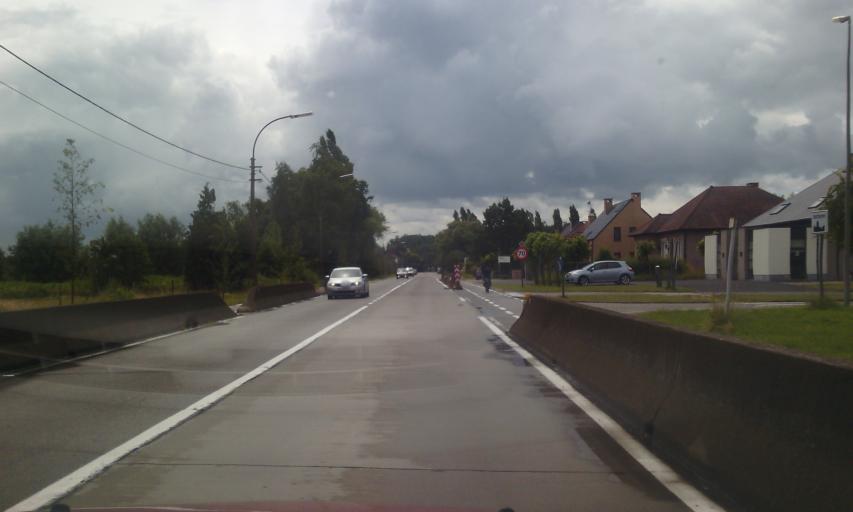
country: BE
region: Flanders
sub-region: Provincie Oost-Vlaanderen
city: Wetteren
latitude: 51.0183
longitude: 3.8834
